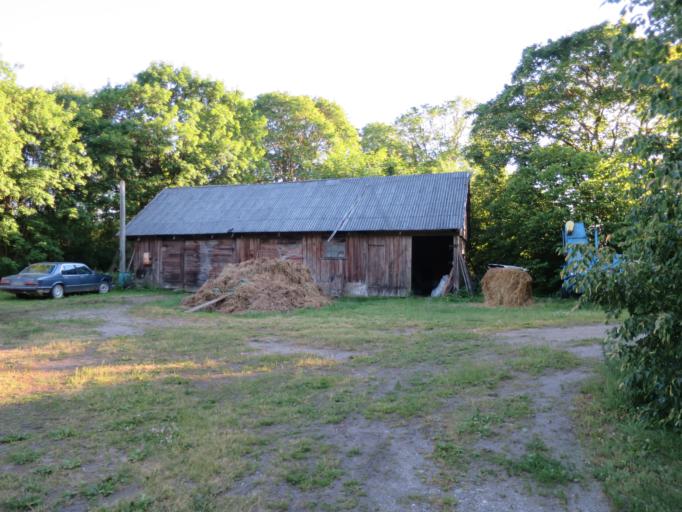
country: LV
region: Rucavas
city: Rucava
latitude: 56.3330
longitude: 21.3081
